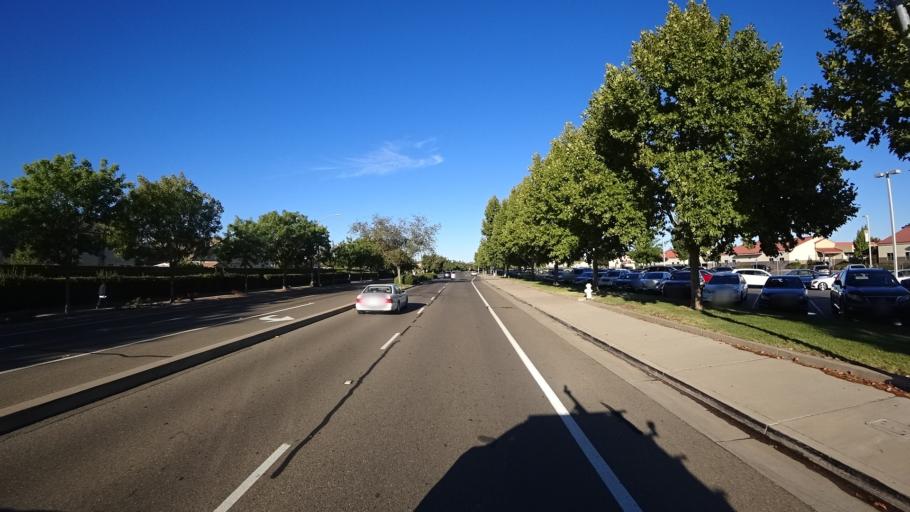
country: US
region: California
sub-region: Sacramento County
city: Laguna
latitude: 38.4481
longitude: -121.3972
